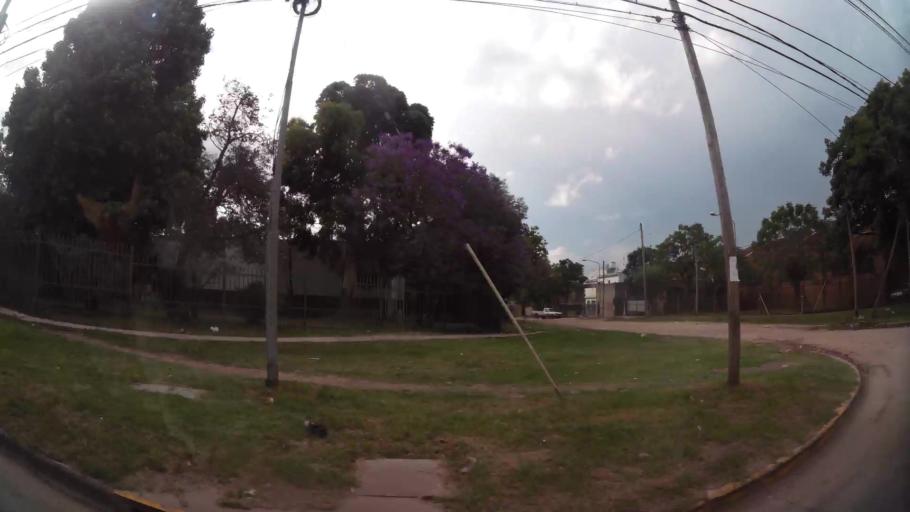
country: AR
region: Buenos Aires
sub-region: Partido de Tigre
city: Tigre
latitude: -34.4789
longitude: -58.6301
